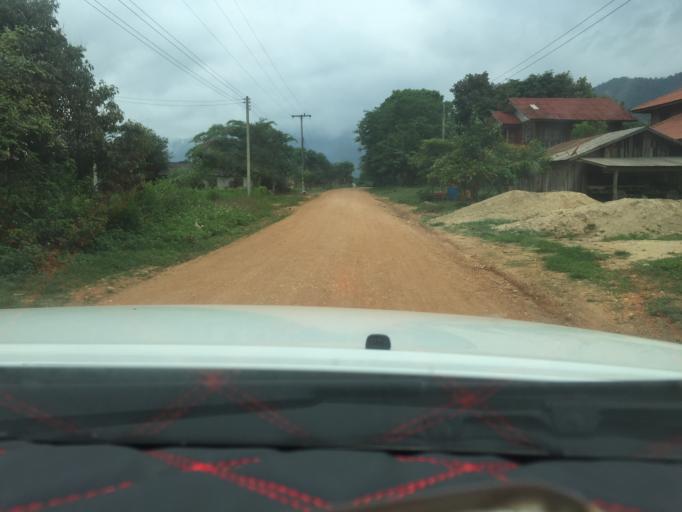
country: TH
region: Phayao
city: Phu Sang
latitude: 19.7384
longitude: 100.4672
